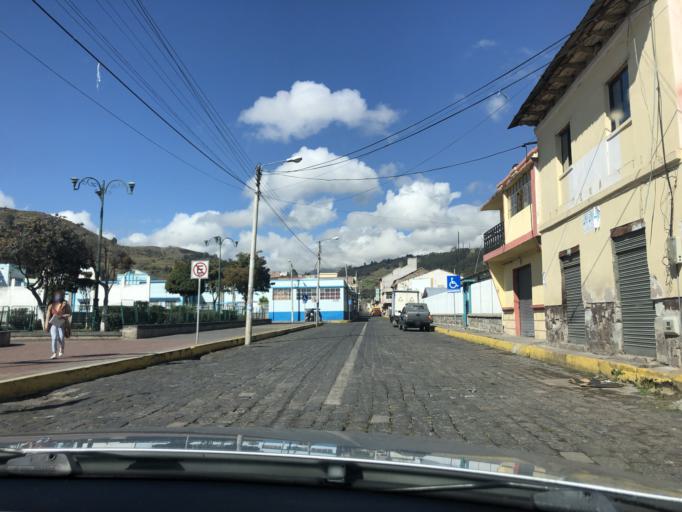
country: EC
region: Chimborazo
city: Riobamba
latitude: -1.7014
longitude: -78.7733
